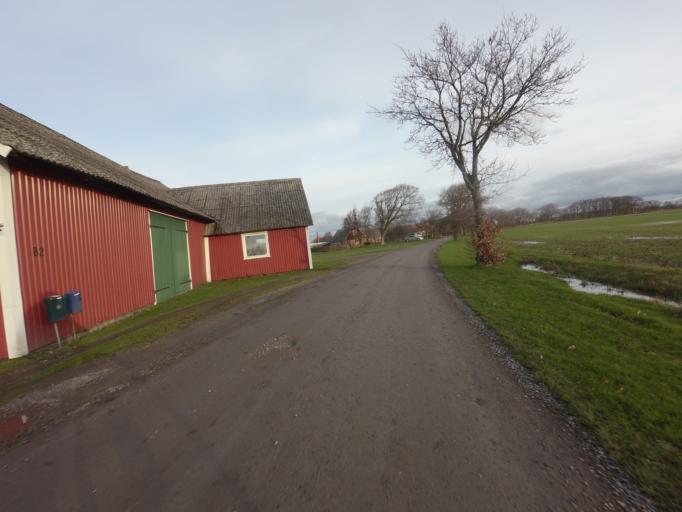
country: SE
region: Skane
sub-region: Hoganas Kommun
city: Hoganas
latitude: 56.1699
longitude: 12.5811
